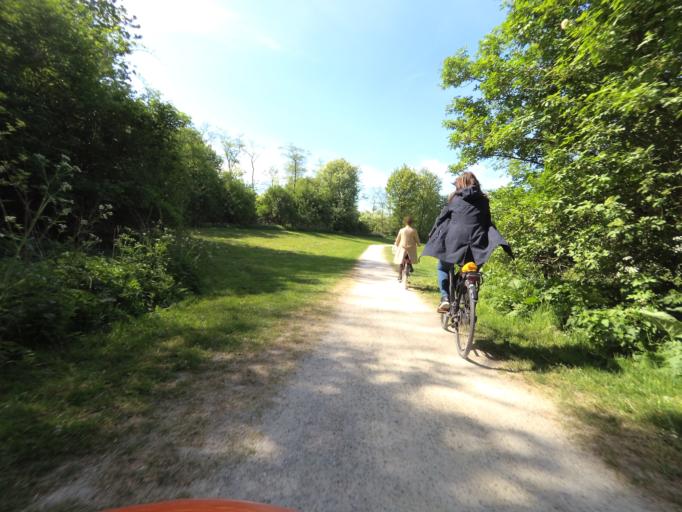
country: NL
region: Flevoland
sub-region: Gemeente Dronten
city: Dronten
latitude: 52.5231
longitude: 5.6845
